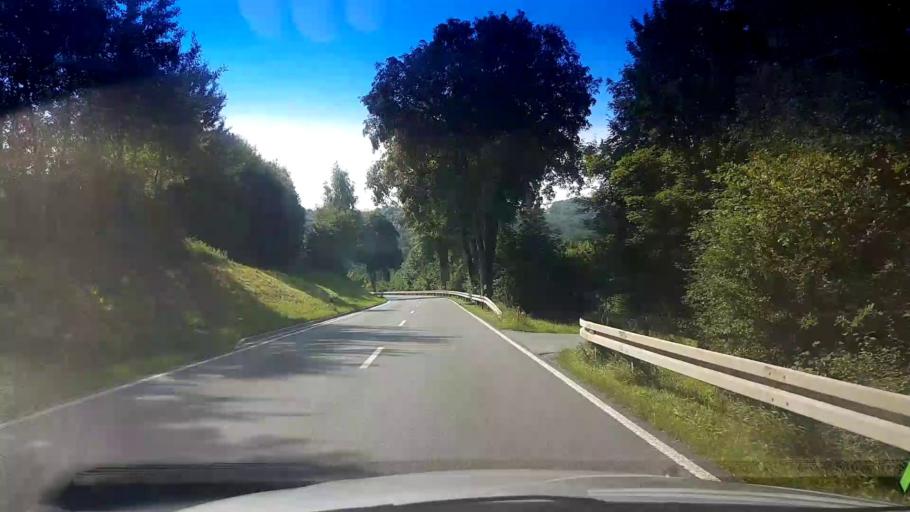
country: DE
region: Bavaria
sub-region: Upper Franconia
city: Hollfeld
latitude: 49.9369
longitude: 11.3447
